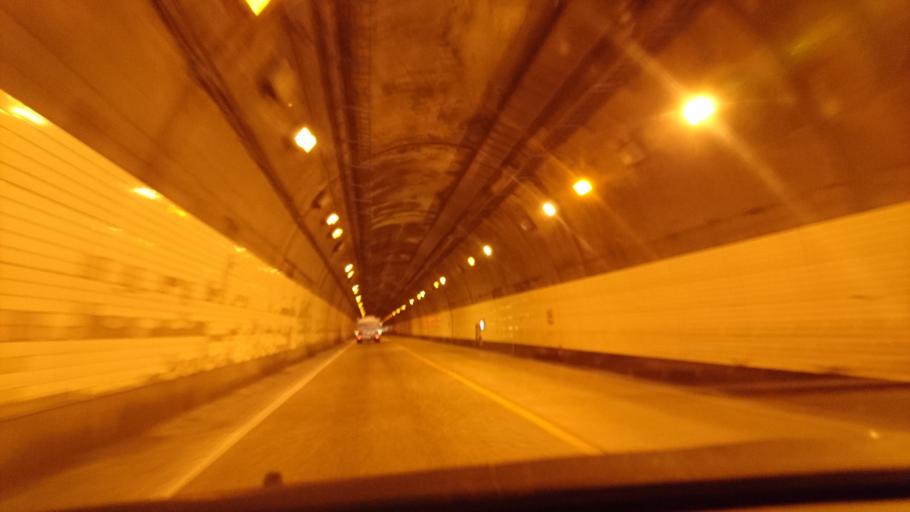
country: JP
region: Iwate
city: Kamaishi
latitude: 39.2312
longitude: 141.8832
